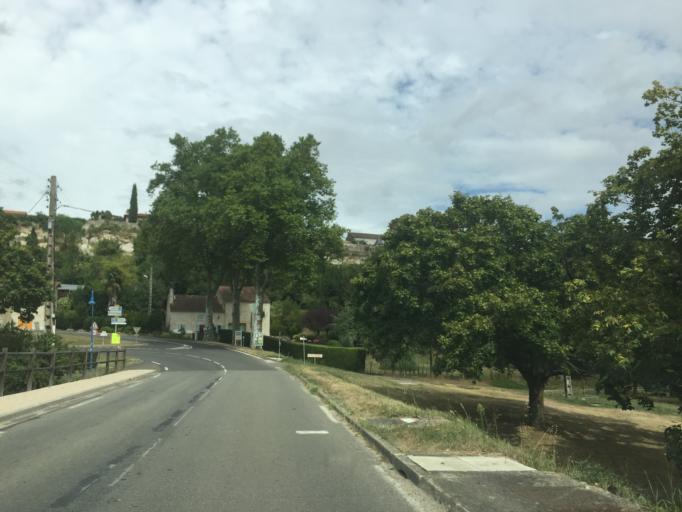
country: FR
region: Midi-Pyrenees
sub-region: Departement du Gers
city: Valence-sur-Baise
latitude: 43.8796
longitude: 0.3806
